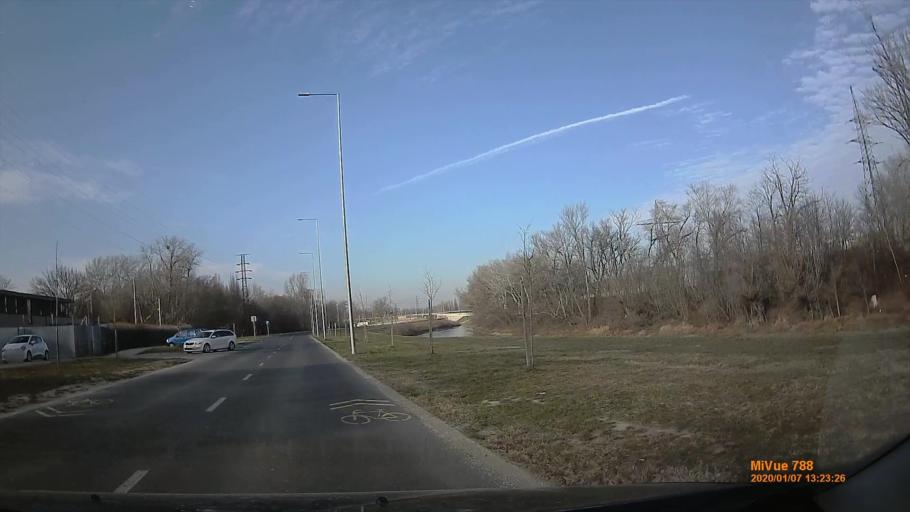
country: HU
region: Gyor-Moson-Sopron
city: Gyor
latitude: 47.6954
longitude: 17.6715
